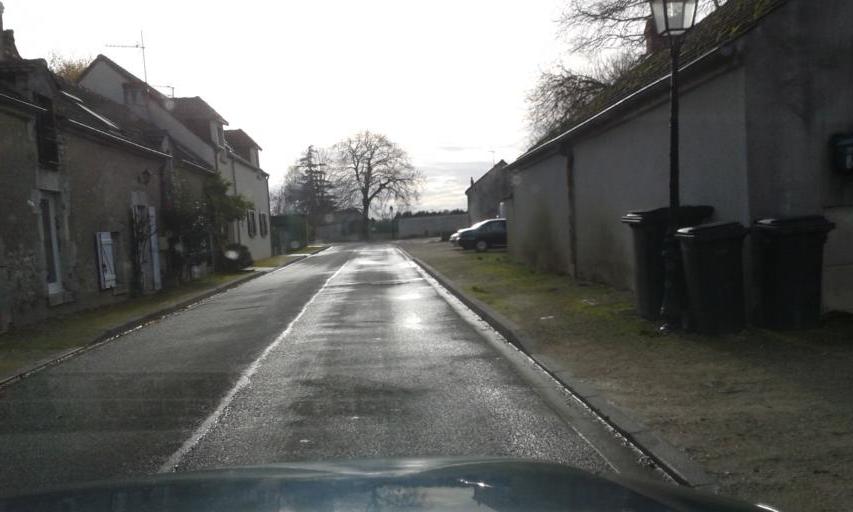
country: FR
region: Centre
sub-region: Departement du Loiret
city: Beaugency
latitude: 47.8072
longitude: 1.6346
